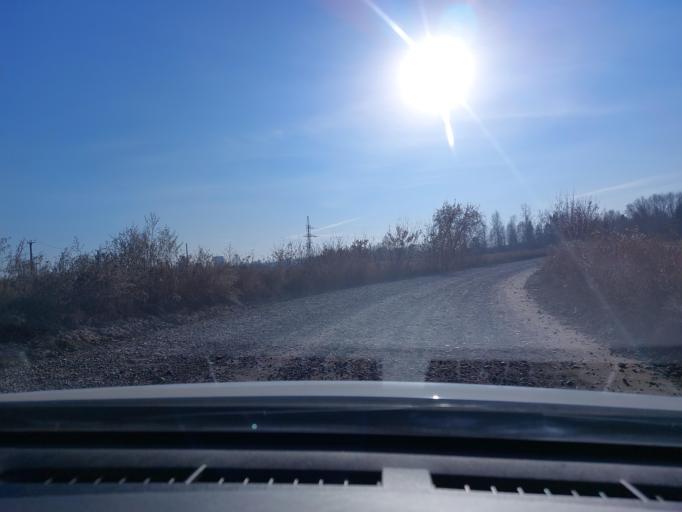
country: RU
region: Irkutsk
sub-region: Irkutskiy Rayon
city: Irkutsk
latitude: 52.3040
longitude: 104.2763
